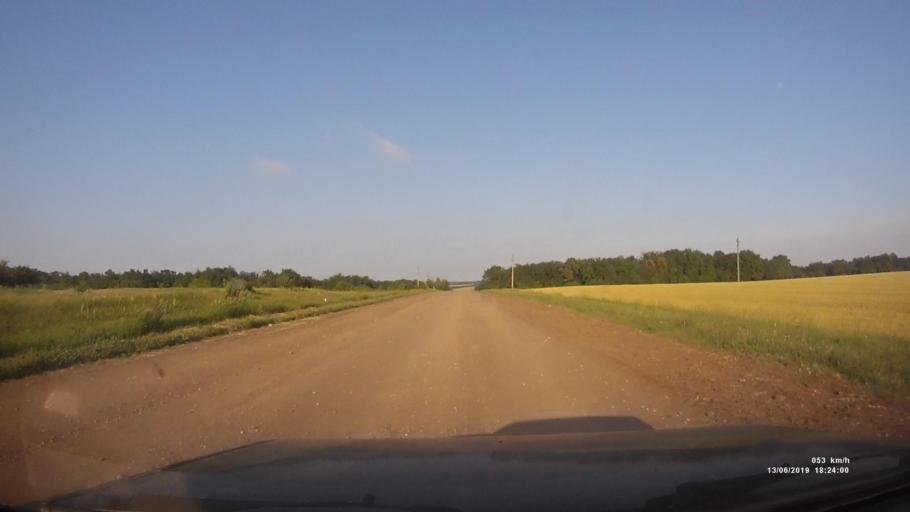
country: RU
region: Rostov
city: Kazanskaya
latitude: 49.8523
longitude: 41.2851
